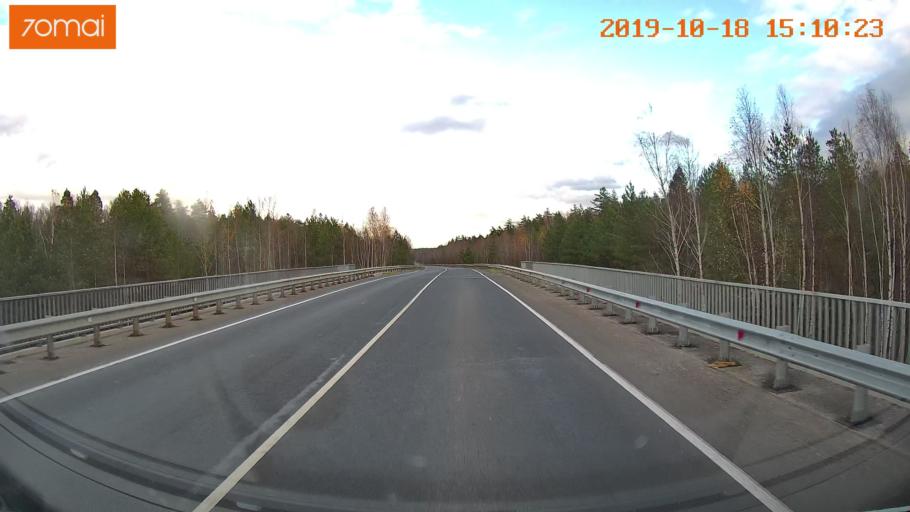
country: RU
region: Vladimir
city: Gus'-Khrustal'nyy
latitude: 55.5679
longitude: 40.6428
